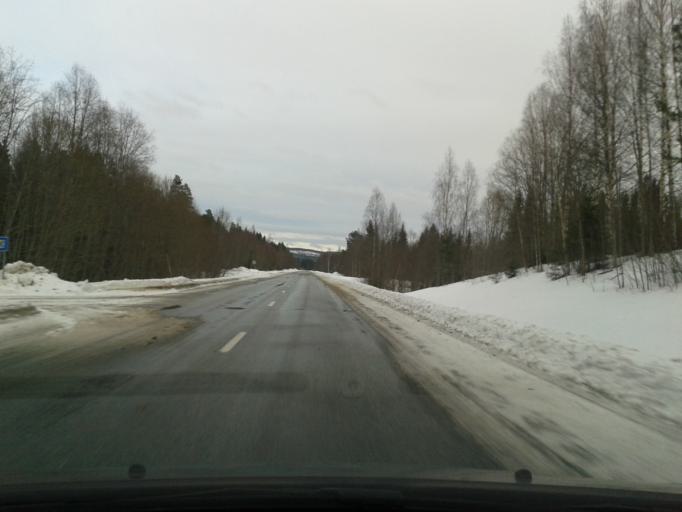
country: SE
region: Vaesternorrland
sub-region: Solleftea Kommun
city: As
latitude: 63.5805
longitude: 16.8254
